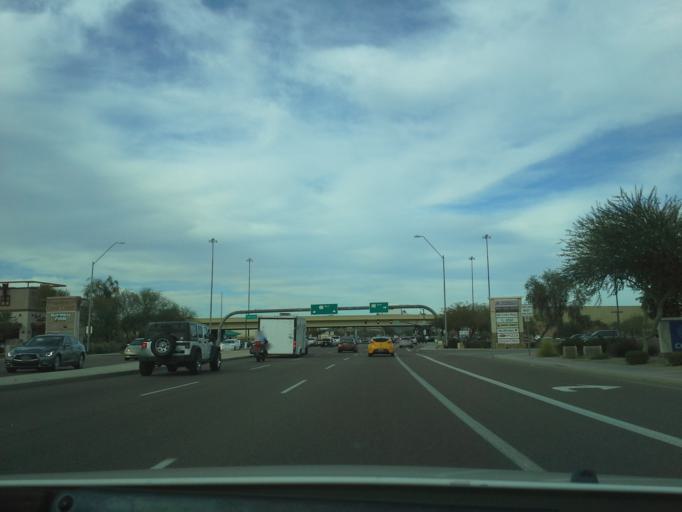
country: US
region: Arizona
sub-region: Maricopa County
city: Paradise Valley
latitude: 33.6703
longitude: -112.0308
